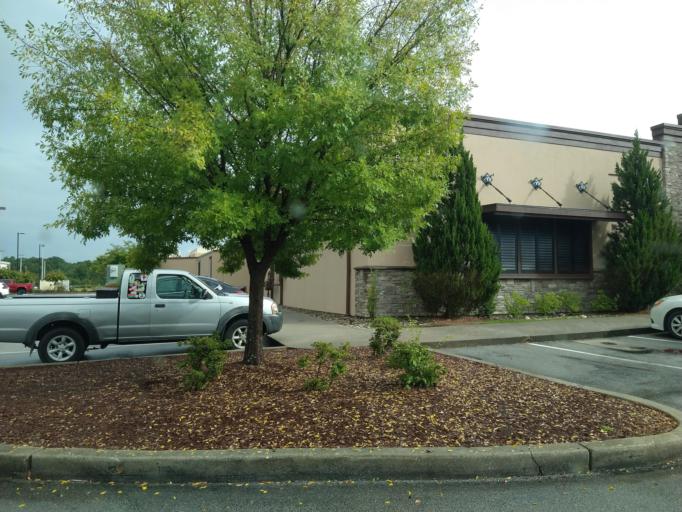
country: US
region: North Carolina
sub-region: Onslow County
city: Pumpkin Center
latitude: 34.7969
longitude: -77.4102
